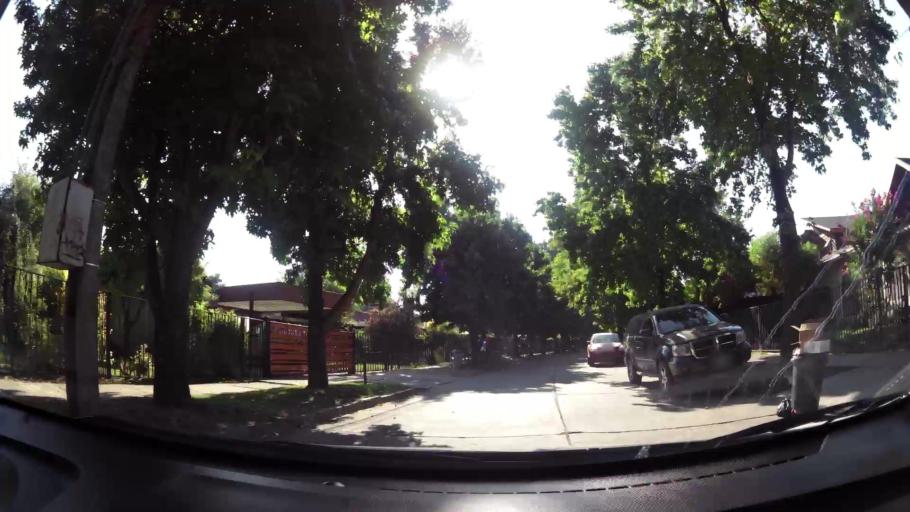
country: CL
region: Maule
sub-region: Provincia de Talca
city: Talca
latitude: -35.4159
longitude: -71.6691
